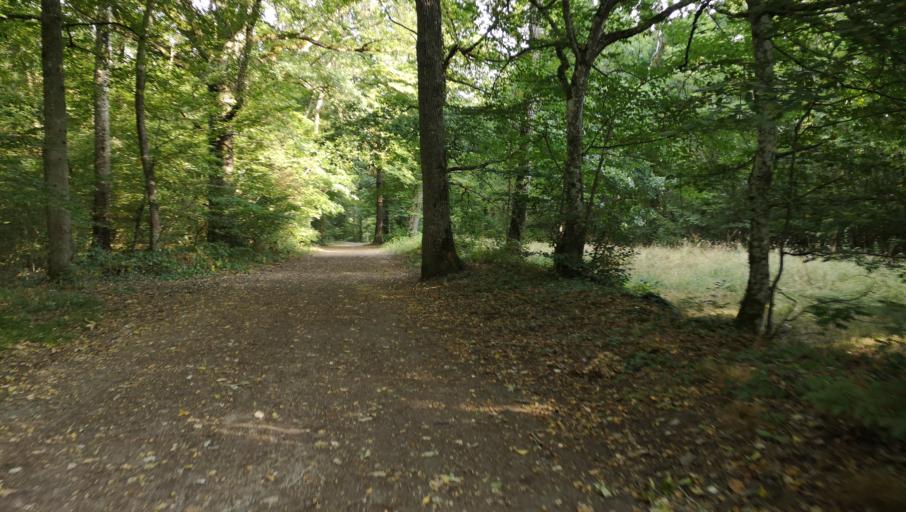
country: FR
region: Centre
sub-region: Departement du Loiret
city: Boigny-sur-Bionne
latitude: 47.9363
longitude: 1.9985
